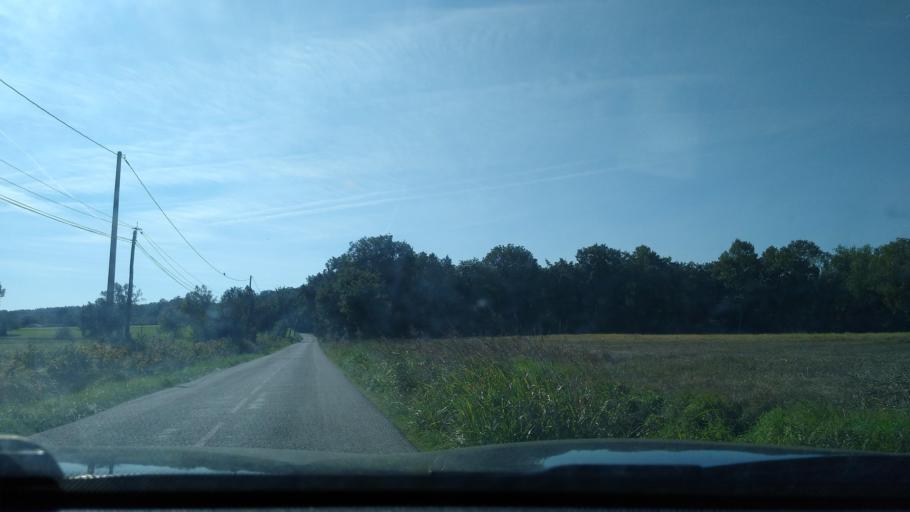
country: FR
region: Midi-Pyrenees
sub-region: Departement de la Haute-Garonne
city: Grenade
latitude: 43.7531
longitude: 1.2543
